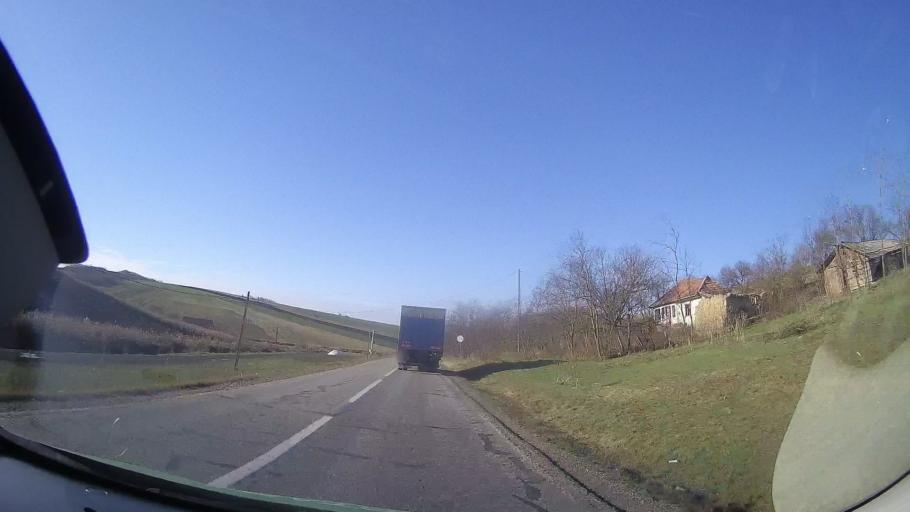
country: RO
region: Cluj
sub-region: Comuna Camarasu
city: Camarasu
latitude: 46.7979
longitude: 24.1674
